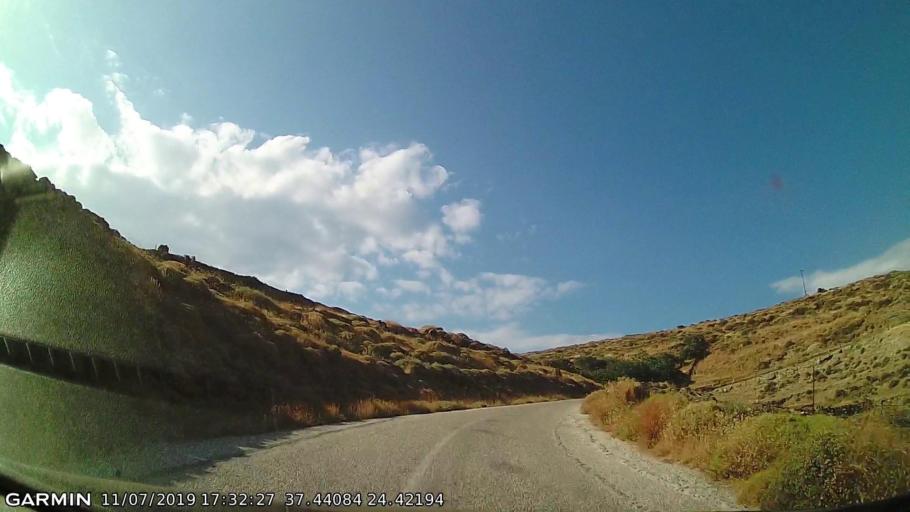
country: GR
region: South Aegean
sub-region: Nomos Kykladon
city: Kythnos
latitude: 37.4407
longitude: 24.4222
